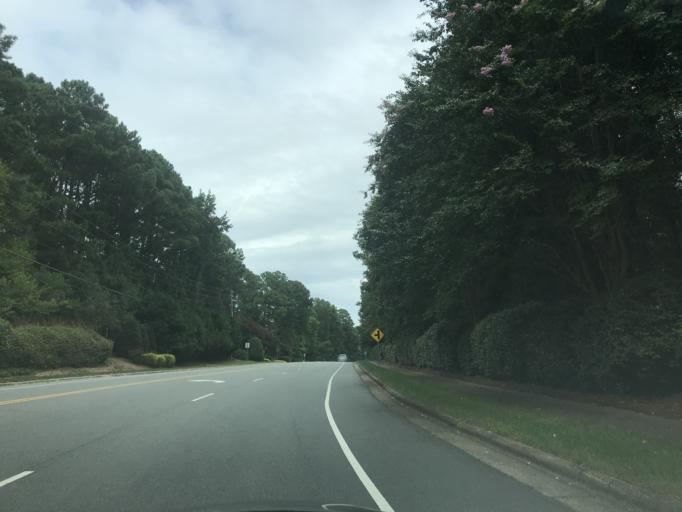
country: US
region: North Carolina
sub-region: Wake County
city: Apex
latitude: 35.7494
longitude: -78.8142
